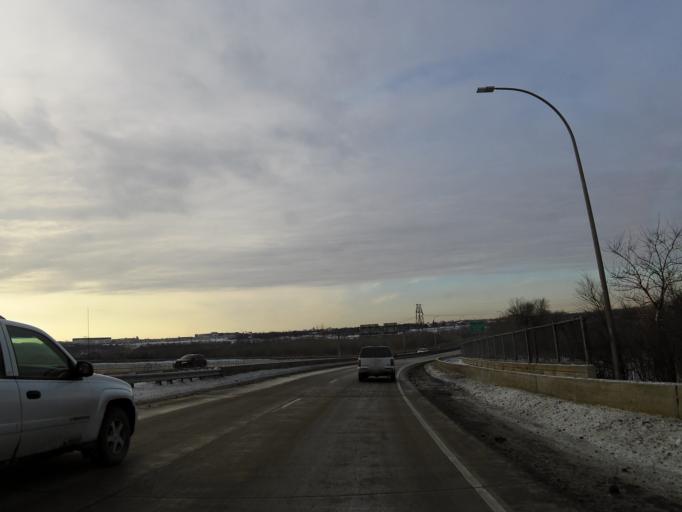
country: US
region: Minnesota
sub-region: Dakota County
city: Mendota Heights
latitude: 44.8830
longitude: -93.1692
